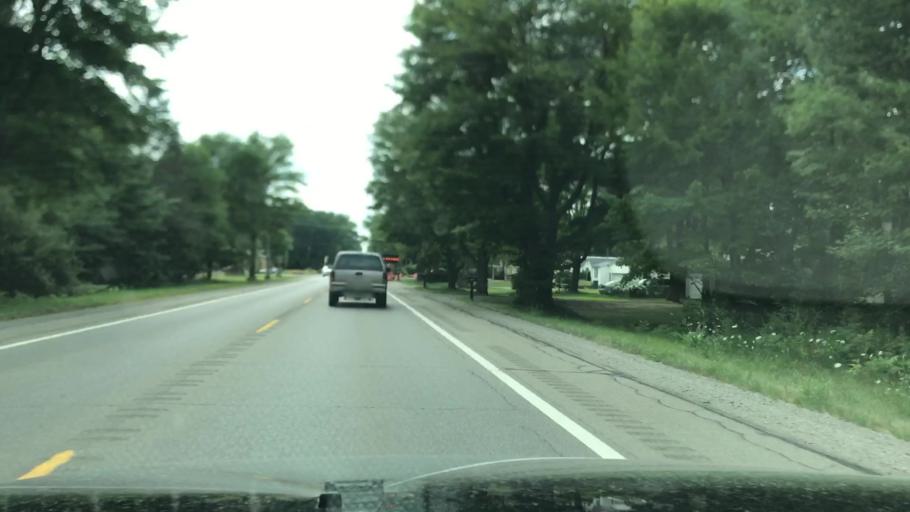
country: US
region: Michigan
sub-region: Muskegon County
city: Fruitport
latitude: 43.0739
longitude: -86.1248
